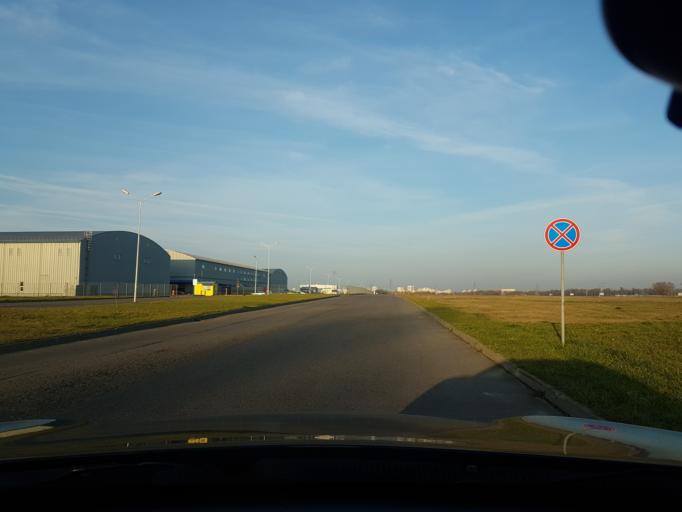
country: BY
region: Minsk
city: Shchomyslitsa
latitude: 53.8234
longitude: 27.4321
